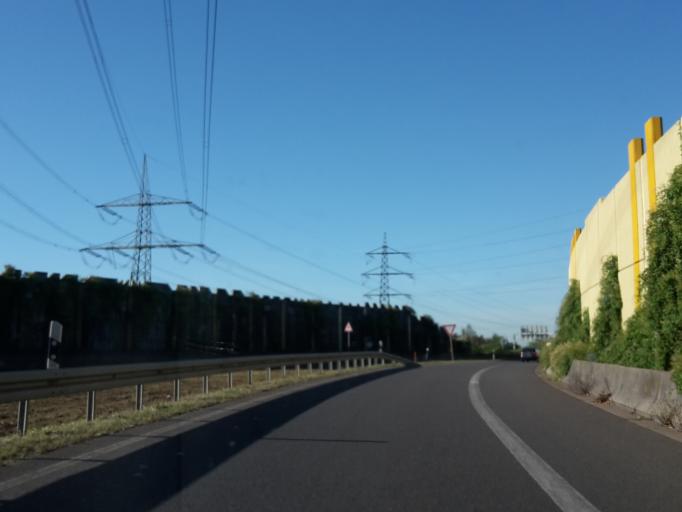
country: DE
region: Hesse
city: Viernheim
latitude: 49.5253
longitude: 8.5609
